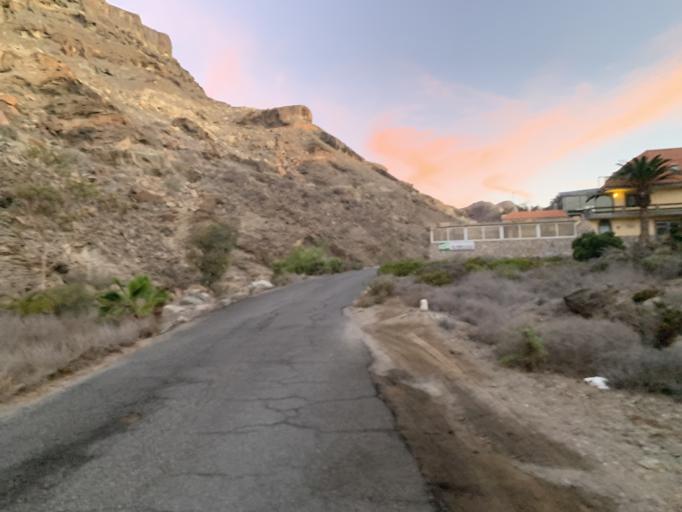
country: ES
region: Canary Islands
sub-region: Provincia de Las Palmas
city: Puerto Rico
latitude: 27.8047
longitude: -15.7316
